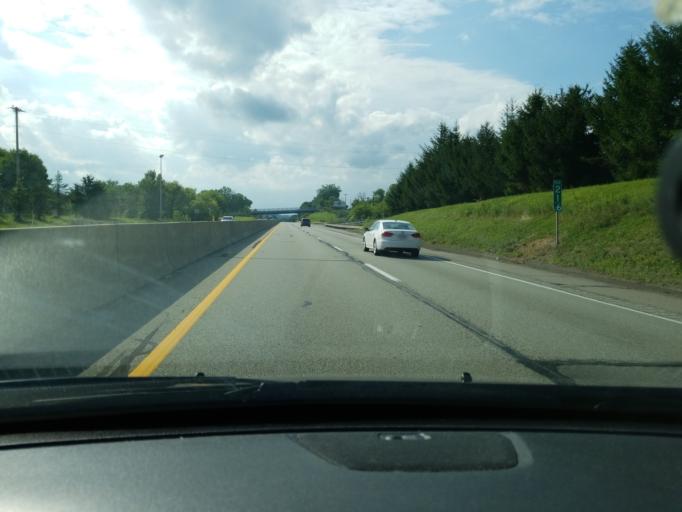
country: US
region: Pennsylvania
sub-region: Butler County
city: Zelienople
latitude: 40.7435
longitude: -80.1966
